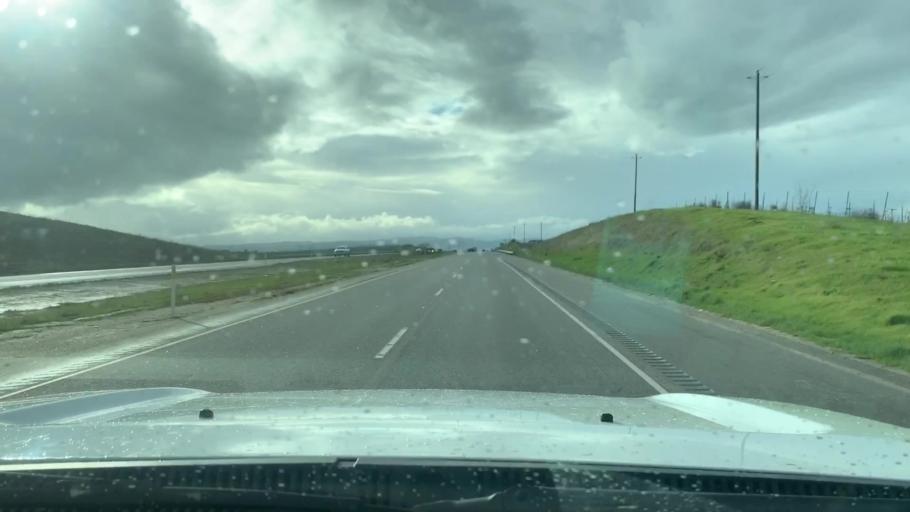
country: US
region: California
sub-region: San Luis Obispo County
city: Paso Robles
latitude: 35.6598
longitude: -120.5530
